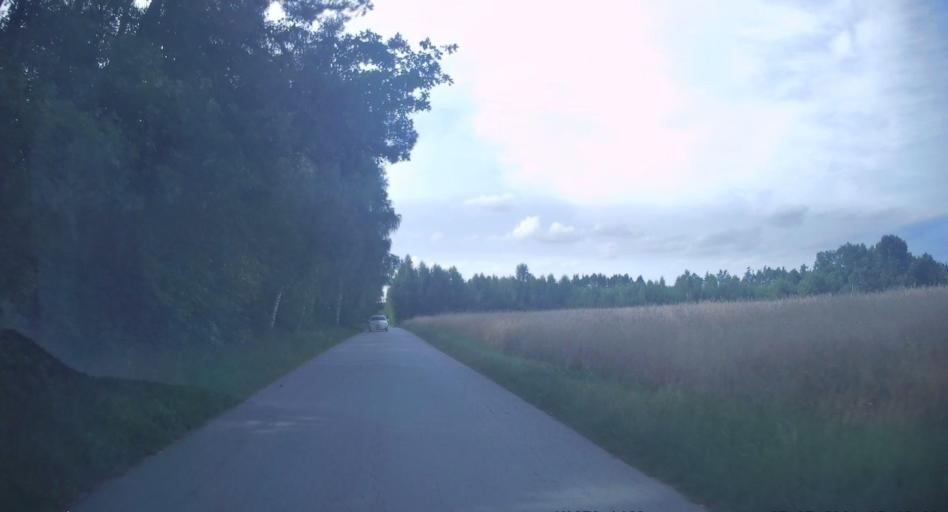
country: PL
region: Lodz Voivodeship
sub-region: Powiat rawski
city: Rawa Mazowiecka
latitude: 51.6969
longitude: 20.2501
